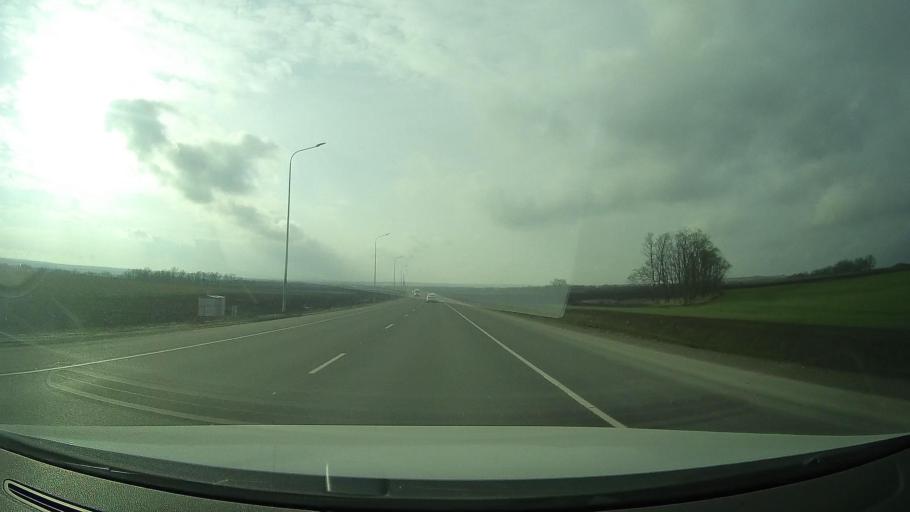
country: RU
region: Rostov
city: Grushevskaya
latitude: 47.4661
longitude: 39.8951
